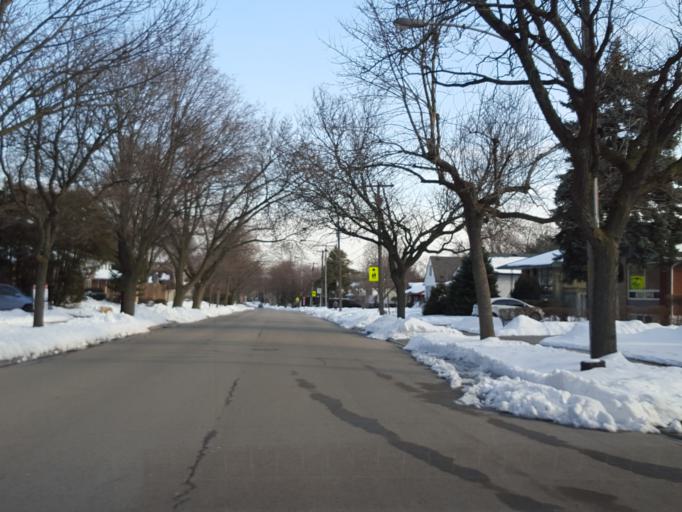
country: CA
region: Ontario
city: Burlington
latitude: 43.3483
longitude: -79.7886
